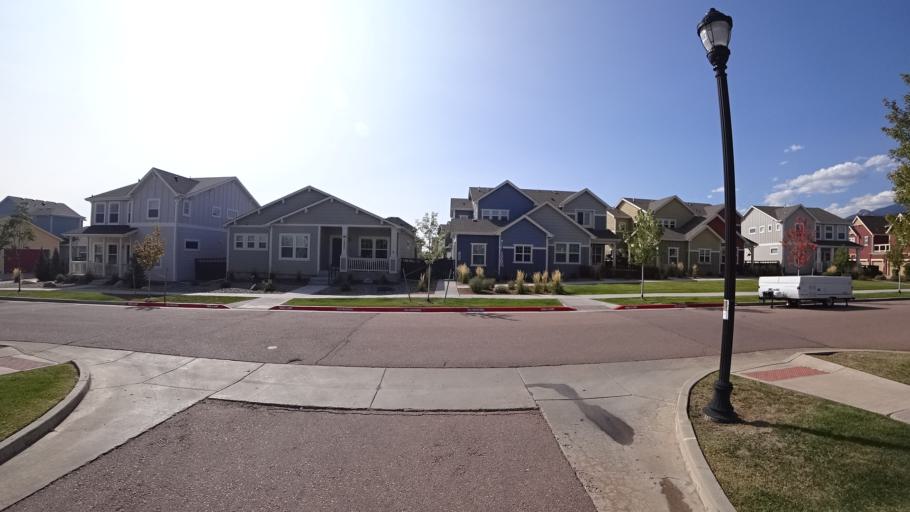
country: US
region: Colorado
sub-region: El Paso County
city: Colorado Springs
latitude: 38.8301
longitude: -104.8516
